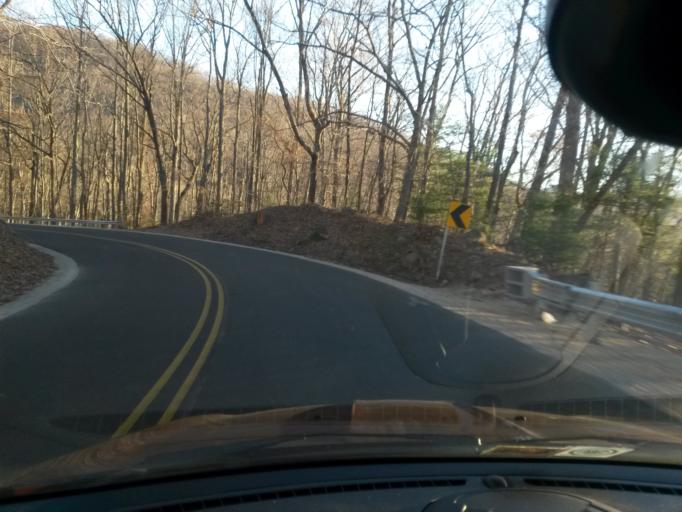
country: US
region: Virginia
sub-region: City of Buena Vista
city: Buena Vista
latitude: 37.7499
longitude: -79.2851
